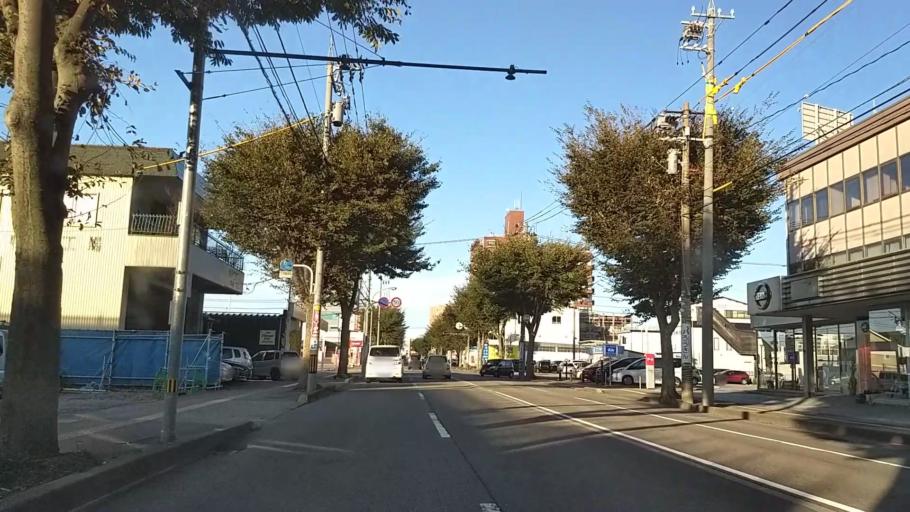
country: JP
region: Ishikawa
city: Nonoichi
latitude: 36.5608
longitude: 136.6398
